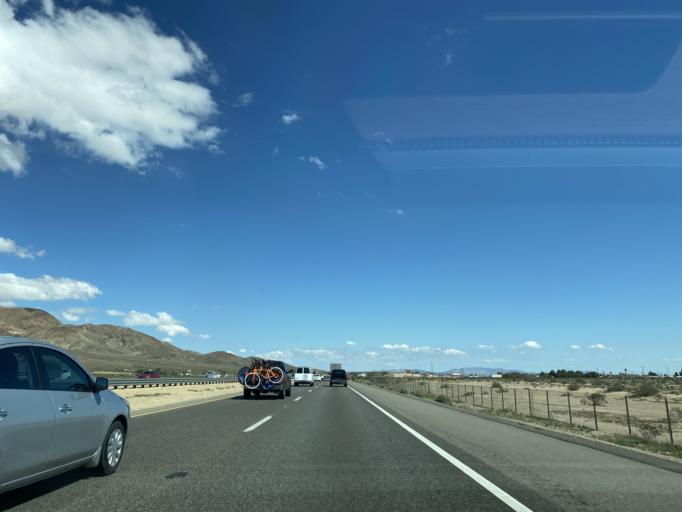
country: US
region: California
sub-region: San Bernardino County
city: Barstow
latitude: 34.9099
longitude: -116.8295
